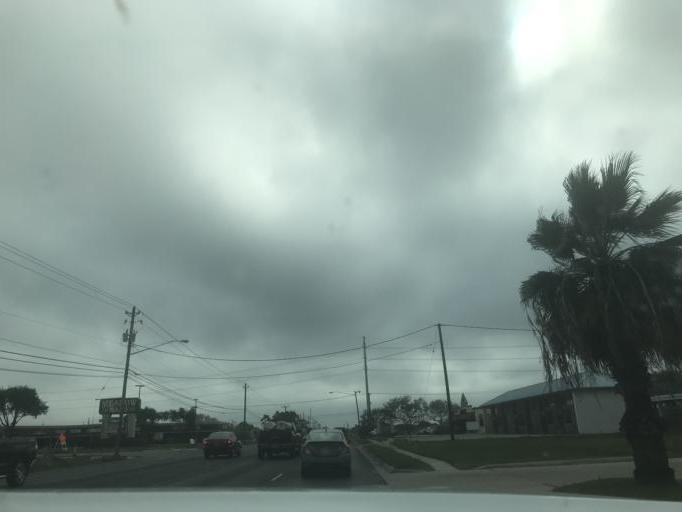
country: US
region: Texas
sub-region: Nueces County
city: Corpus Christi
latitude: 27.6898
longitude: -97.3636
